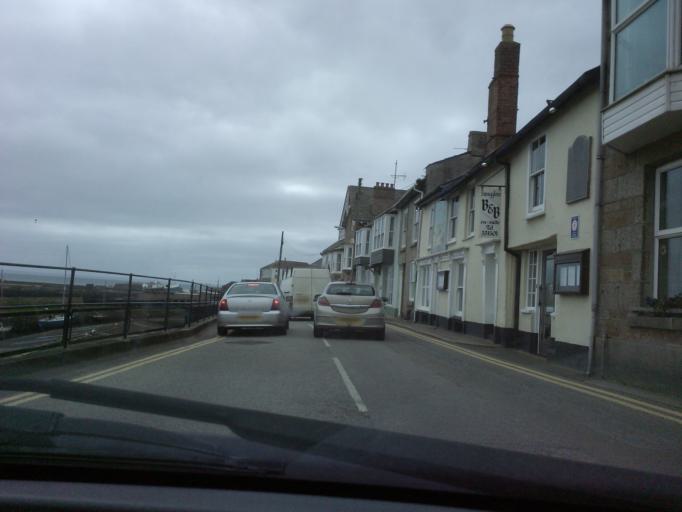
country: GB
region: England
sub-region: Cornwall
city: Penzance
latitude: 50.1028
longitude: -5.5487
